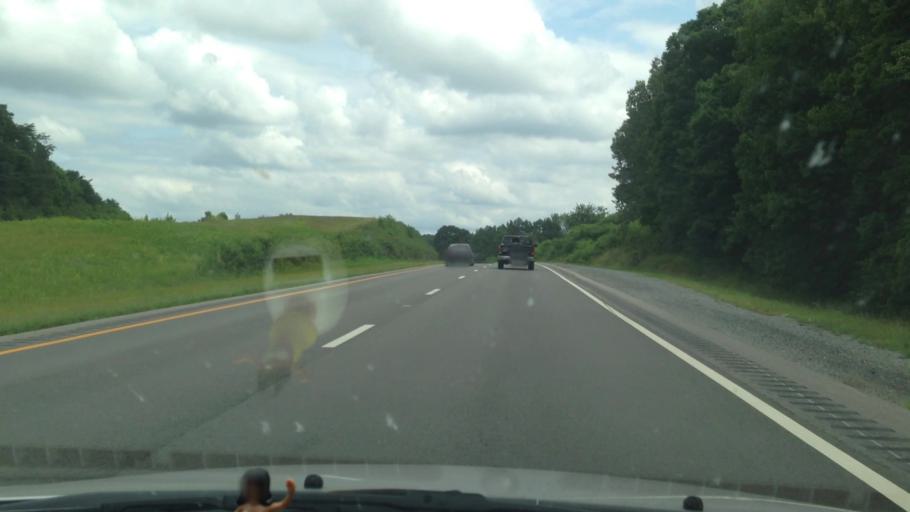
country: US
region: Virginia
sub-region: Pittsylvania County
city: Gretna
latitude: 36.9723
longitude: -79.3585
